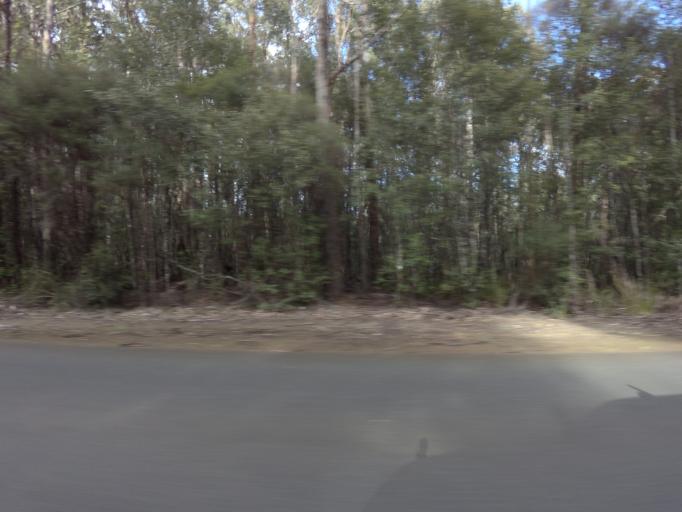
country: AU
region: Tasmania
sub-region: Huon Valley
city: Geeveston
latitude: -43.3807
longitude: 146.9602
